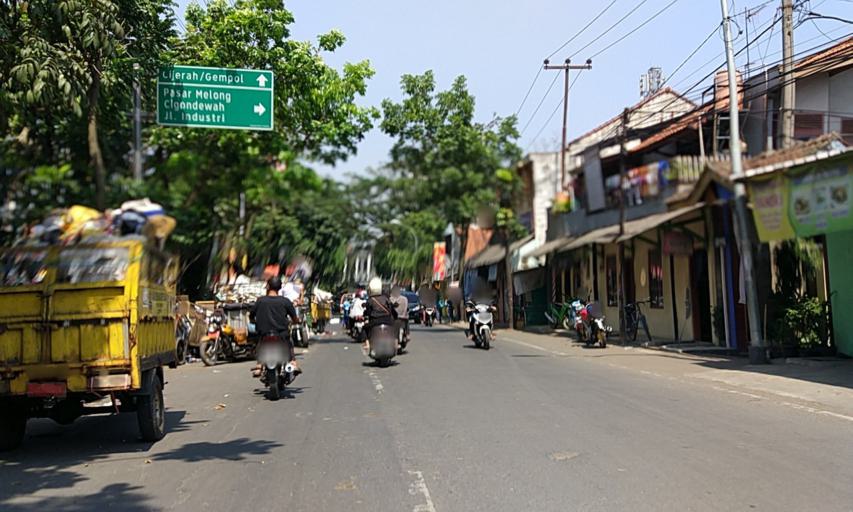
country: ID
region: West Java
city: Margahayukencana
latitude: -6.9230
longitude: 107.5629
